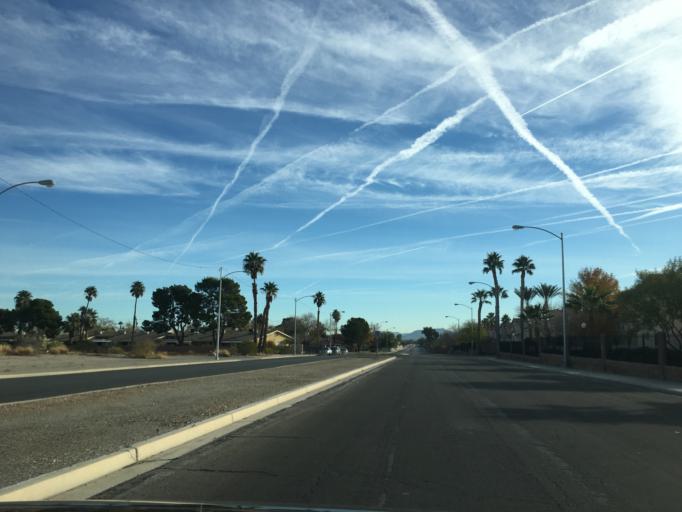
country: US
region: Nevada
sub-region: Clark County
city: Enterprise
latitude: 36.0173
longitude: -115.1709
